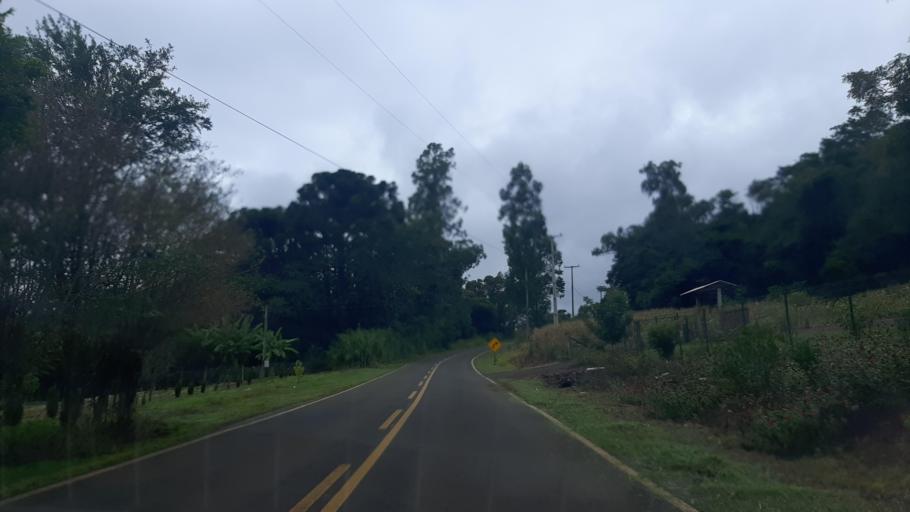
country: BR
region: Parana
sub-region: Ampere
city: Ampere
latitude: -25.9370
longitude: -53.4631
